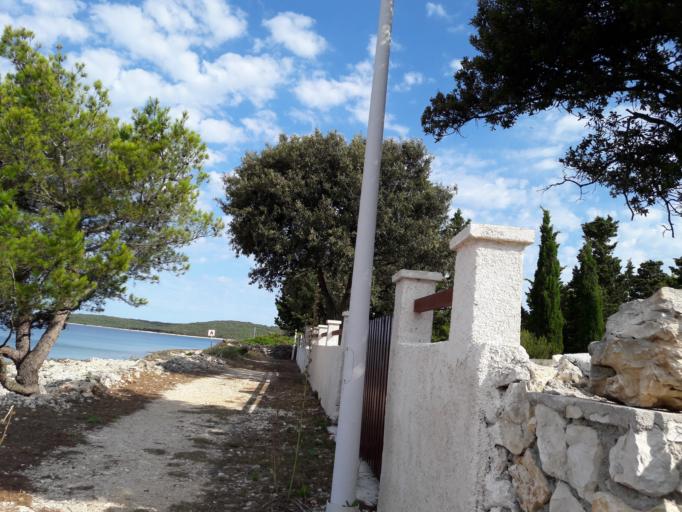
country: HR
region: Primorsko-Goranska
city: Mali Losinj
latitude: 44.3805
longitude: 14.6880
